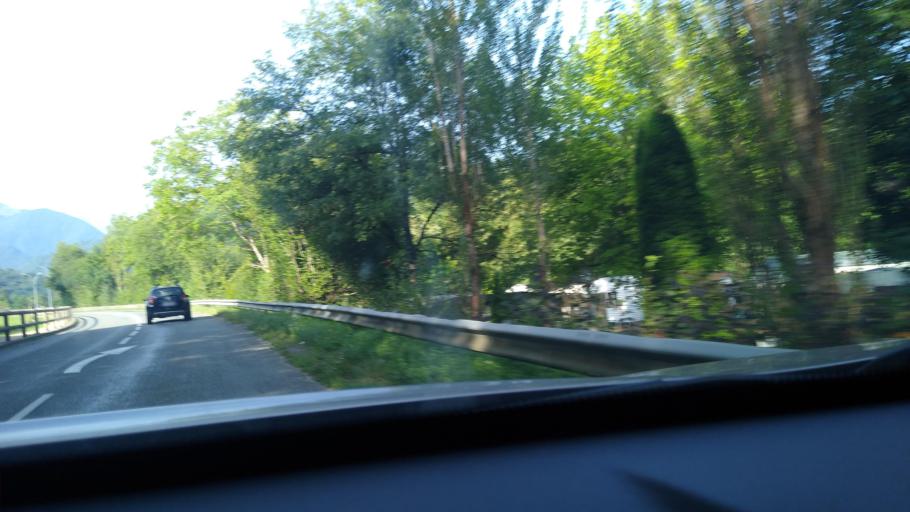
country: FR
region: Midi-Pyrenees
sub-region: Departement de l'Ariege
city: Saint-Girons
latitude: 42.8697
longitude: 1.2098
